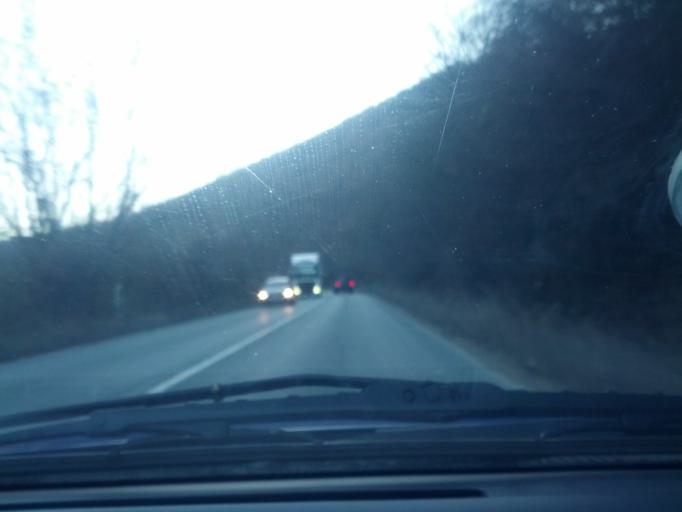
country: BG
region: Vratsa
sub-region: Obshtina Mezdra
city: Mezdra
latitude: 43.0825
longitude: 23.6843
